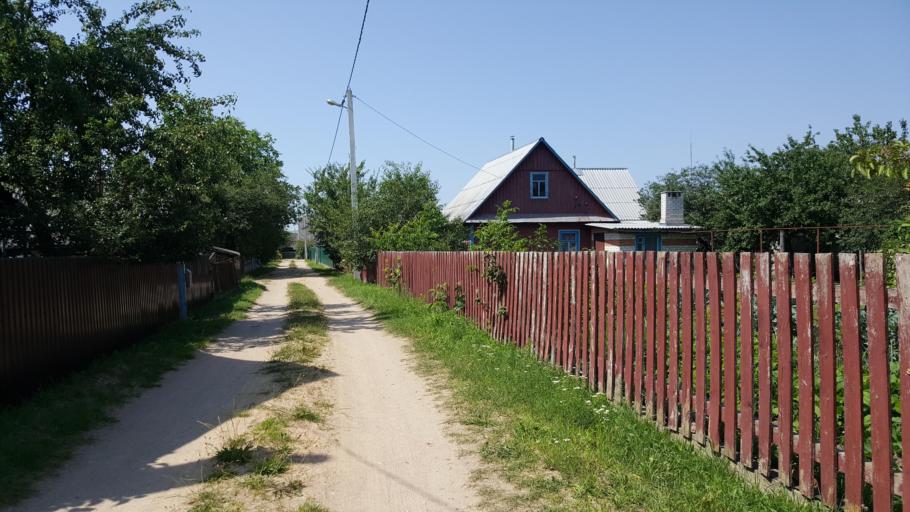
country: BY
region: Brest
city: Zhabinka
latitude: 52.1963
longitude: 23.9946
